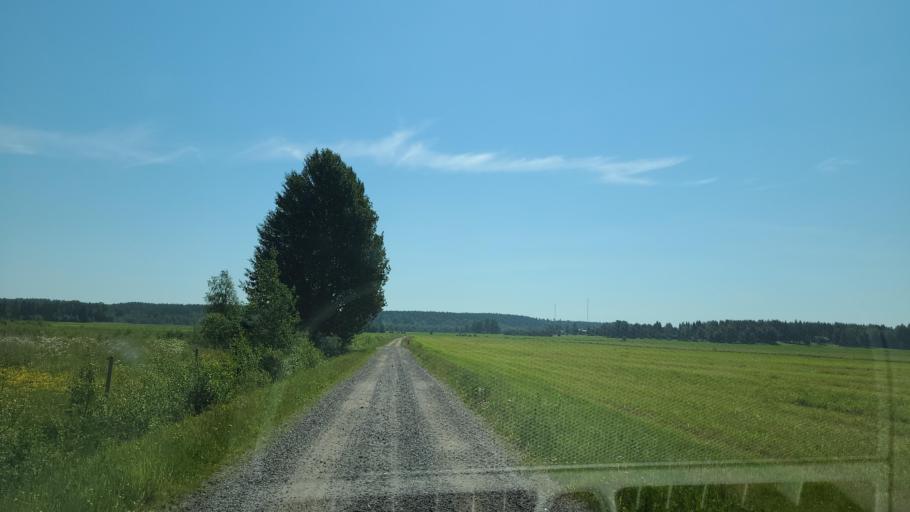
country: SE
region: Vaesterbotten
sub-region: Robertsfors Kommun
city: Robertsfors
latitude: 64.0870
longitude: 20.8516
